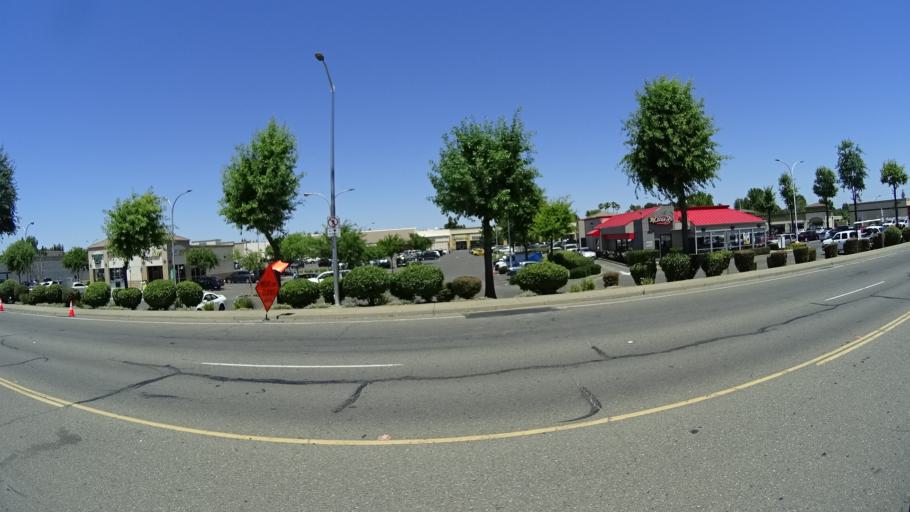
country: US
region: California
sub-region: Sacramento County
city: Rosemont
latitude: 38.5469
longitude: -121.3938
